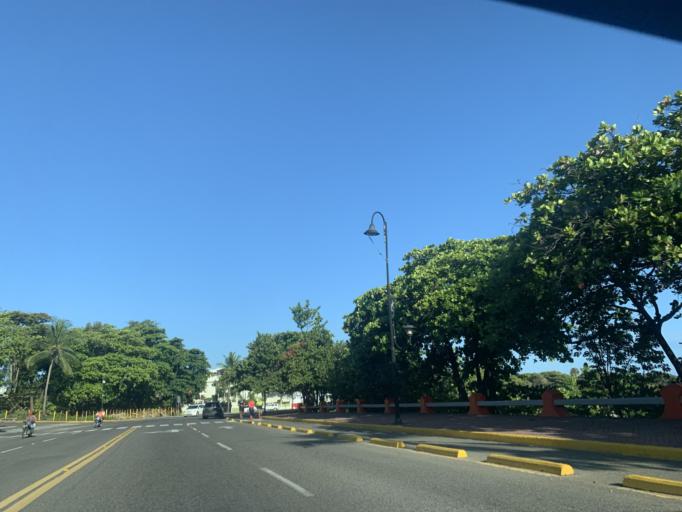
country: DO
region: Puerto Plata
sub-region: Puerto Plata
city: Puerto Plata
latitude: 19.7927
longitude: -70.6769
